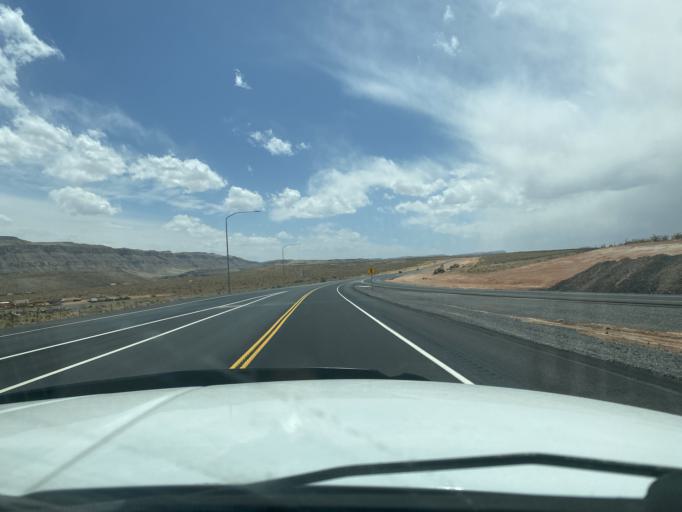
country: US
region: Utah
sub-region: Washington County
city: Hurricane
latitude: 37.1232
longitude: -113.3440
